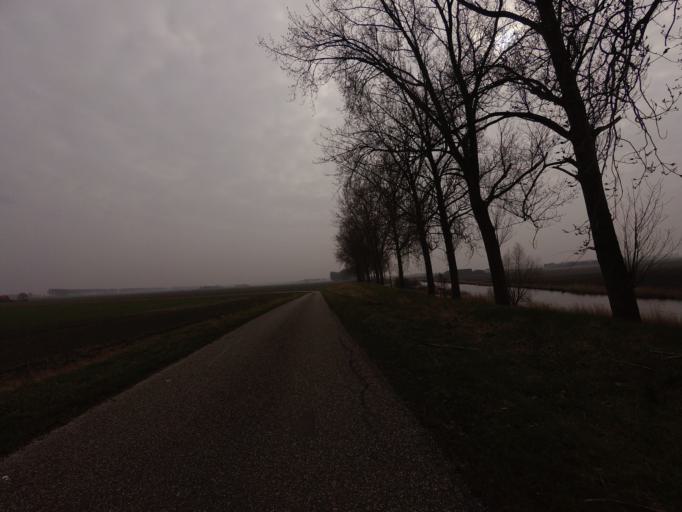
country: NL
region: Zeeland
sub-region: Gemeente Hulst
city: Hulst
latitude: 51.3461
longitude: 4.1082
